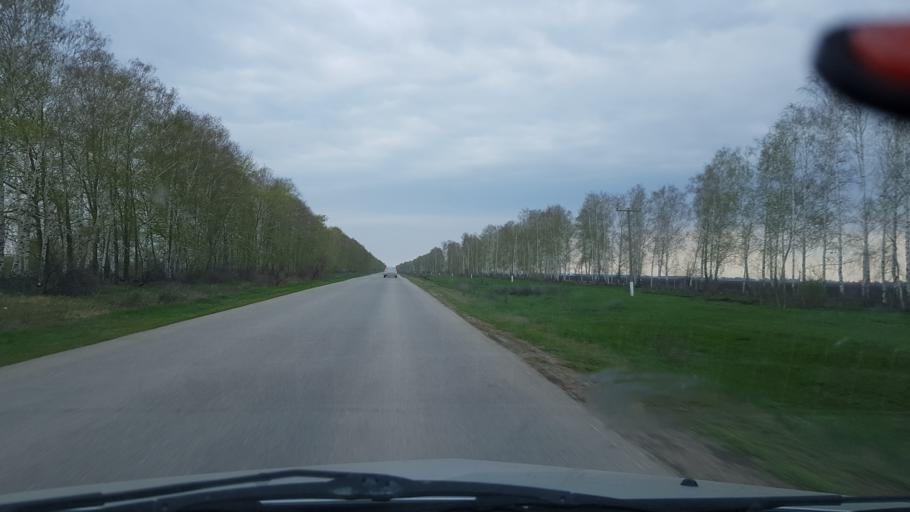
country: RU
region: Samara
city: Tol'yatti
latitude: 53.6592
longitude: 49.2329
